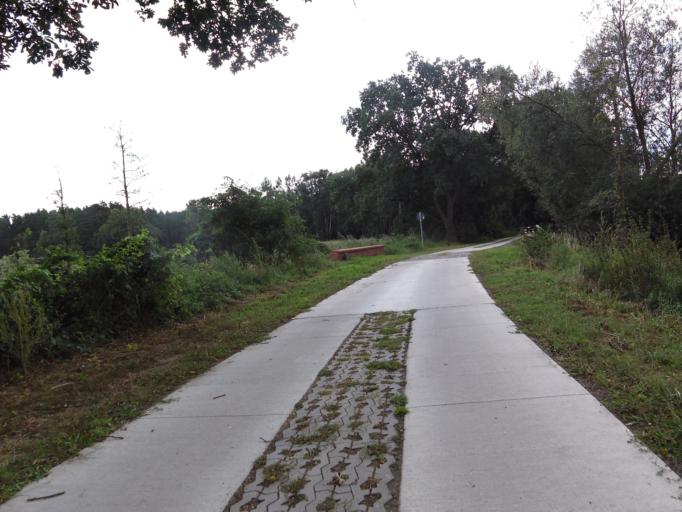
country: DE
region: Saxony-Anhalt
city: Gross Rosenburg
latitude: 51.9546
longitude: 11.9565
